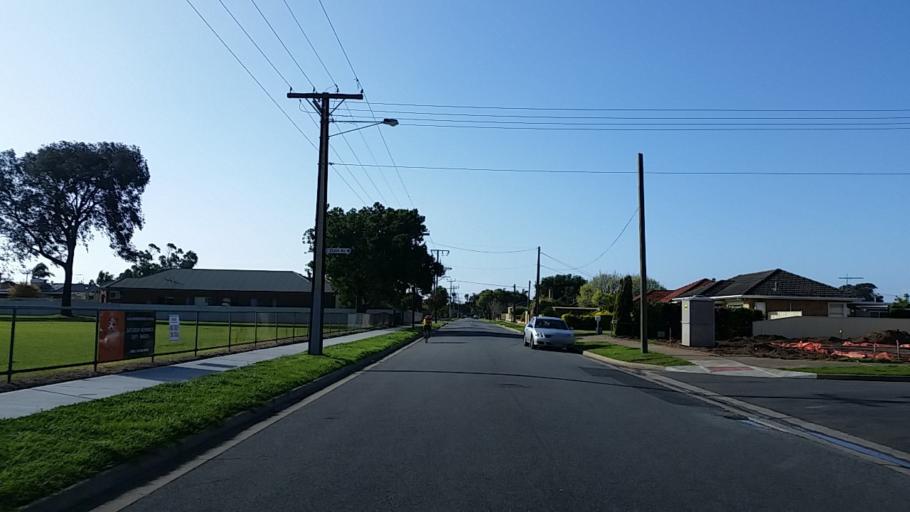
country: AU
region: South Australia
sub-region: Charles Sturt
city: Findon
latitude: -34.8979
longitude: 138.5276
